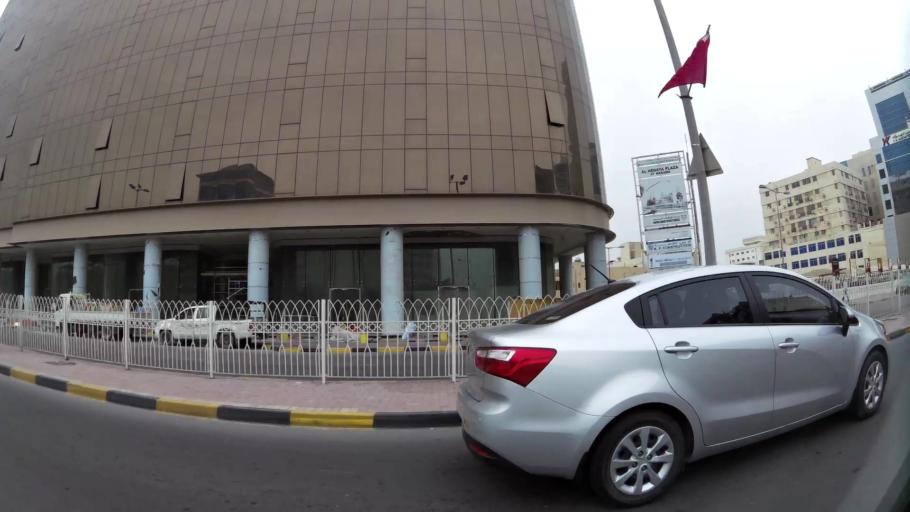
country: BH
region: Manama
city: Manama
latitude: 26.2368
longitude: 50.5789
